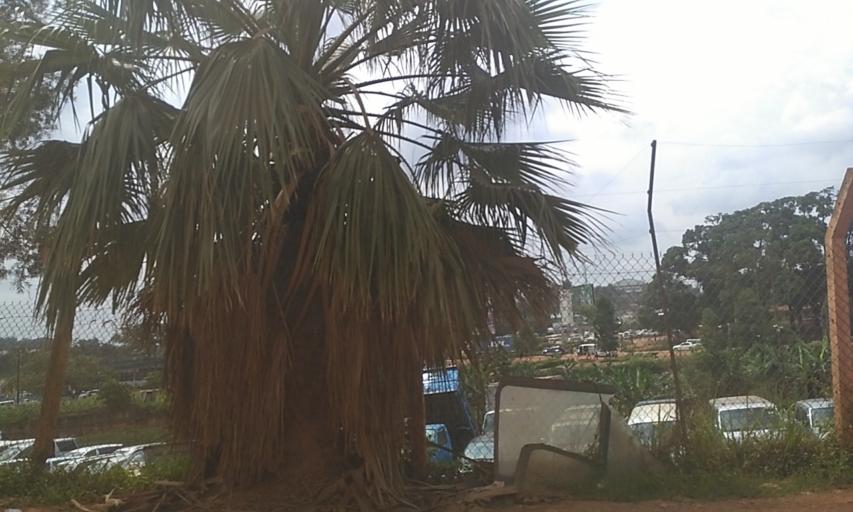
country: UG
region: Central Region
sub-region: Wakiso District
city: Kireka
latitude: 0.3355
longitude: 32.6177
